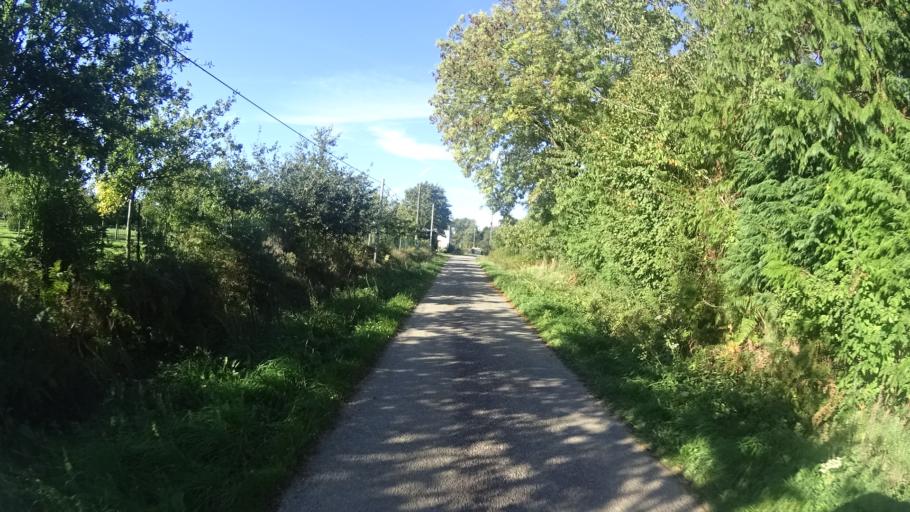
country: FR
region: Brittany
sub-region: Departement du Morbihan
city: Saint-Vincent-sur-Oust
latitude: 47.7055
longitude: -2.1717
